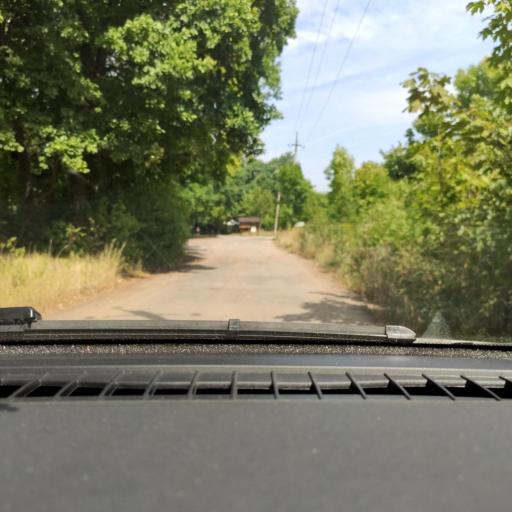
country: RU
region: Voronezj
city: Pridonskoy
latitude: 51.7562
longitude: 39.0792
